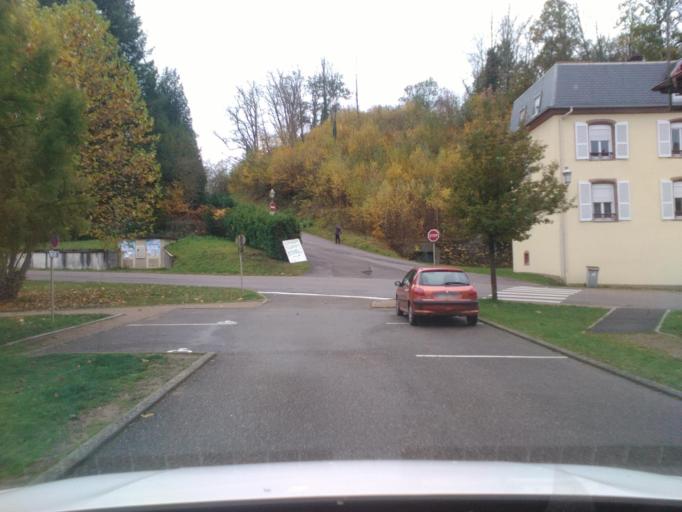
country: FR
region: Lorraine
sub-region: Departement des Vosges
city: Senones
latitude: 48.3959
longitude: 6.9845
